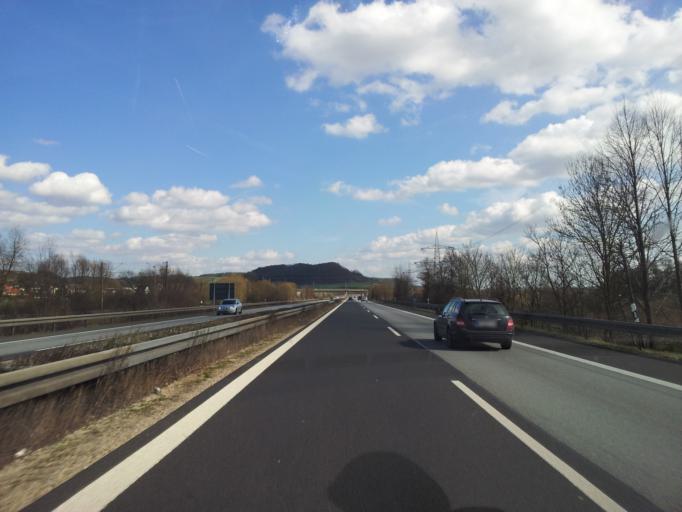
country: DE
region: Bavaria
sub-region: Regierungsbezirk Unterfranken
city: Stettfeld
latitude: 49.9681
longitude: 10.7147
